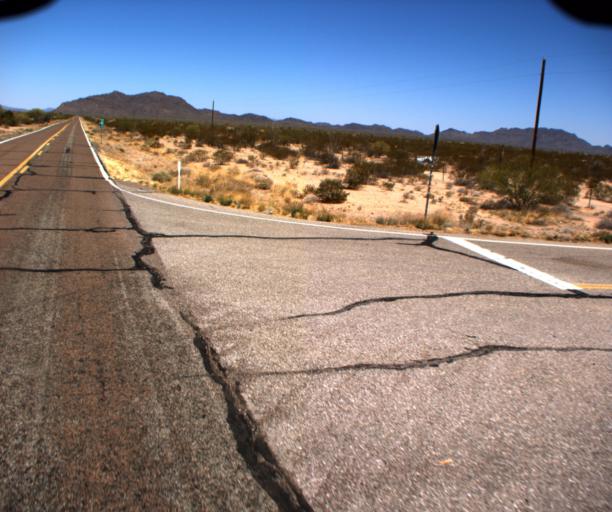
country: US
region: Arizona
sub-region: Pima County
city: Ajo
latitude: 32.2134
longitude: -112.6317
